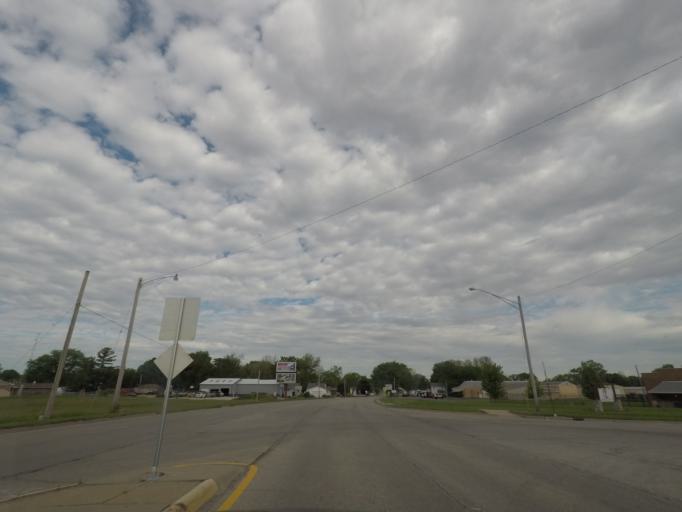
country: US
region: Illinois
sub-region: Logan County
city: Lincoln
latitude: 40.1482
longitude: -89.3520
